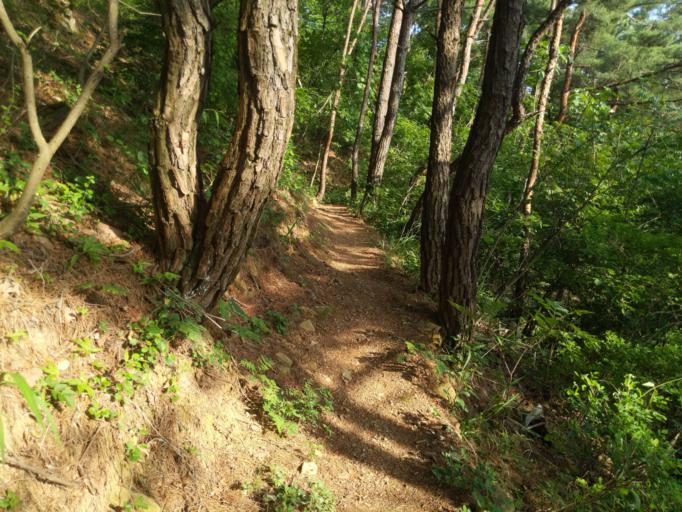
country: KR
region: Daegu
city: Hwawon
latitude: 35.7887
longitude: 128.5403
